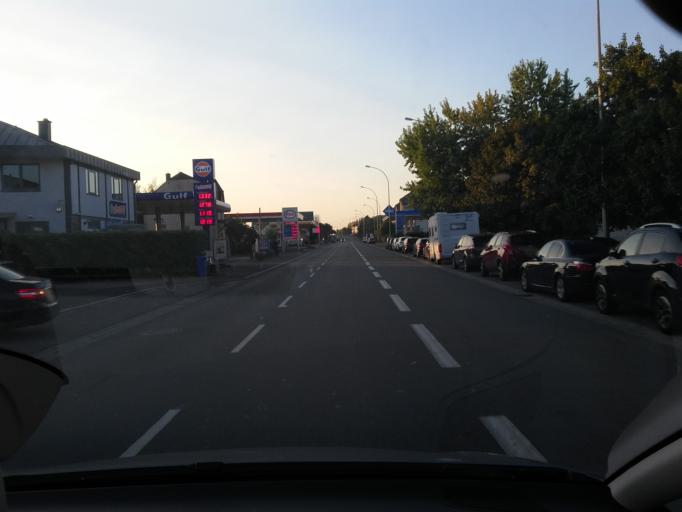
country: LU
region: Luxembourg
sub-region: Canton d'Esch-sur-Alzette
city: Frisange
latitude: 49.5102
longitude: 6.1911
